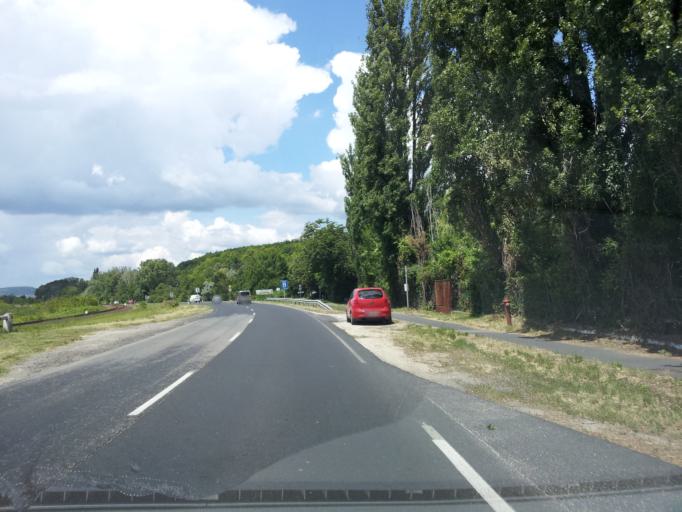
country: HU
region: Veszprem
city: Balatonkenese
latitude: 47.0379
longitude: 18.0842
